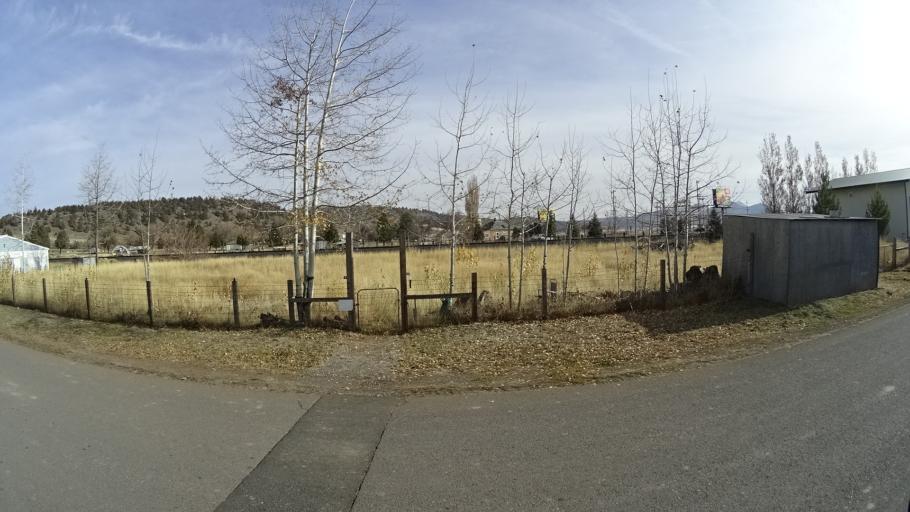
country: US
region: Oregon
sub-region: Klamath County
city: Klamath Falls
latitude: 41.9682
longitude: -121.9146
